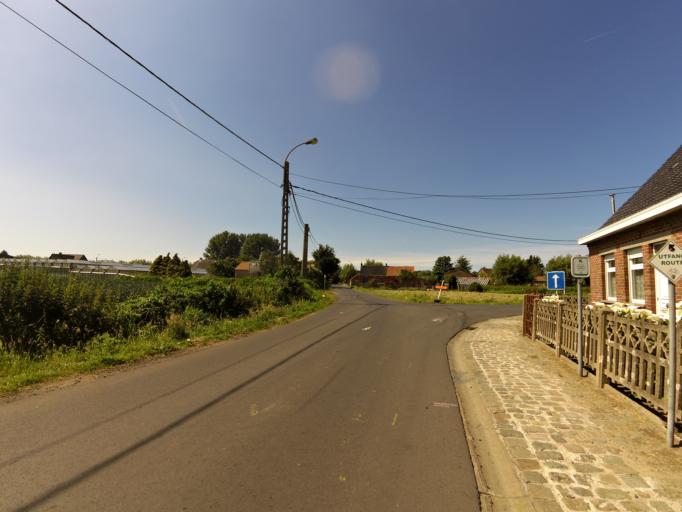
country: BE
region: Flanders
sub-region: Provincie West-Vlaanderen
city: Jabbeke
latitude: 51.1519
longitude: 3.0450
